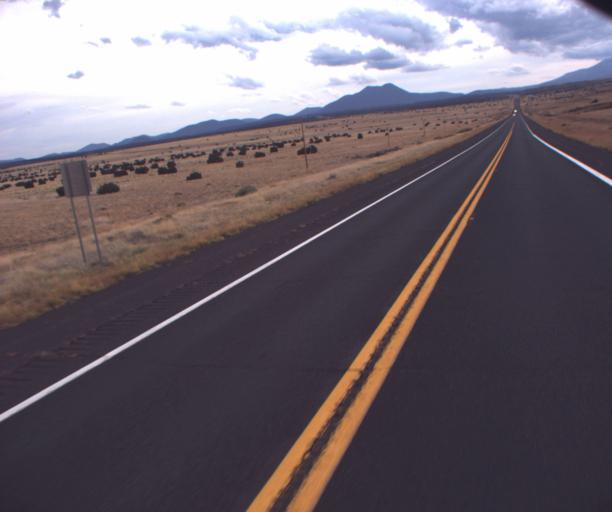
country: US
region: Arizona
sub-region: Coconino County
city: Flagstaff
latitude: 35.5660
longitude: -111.5330
